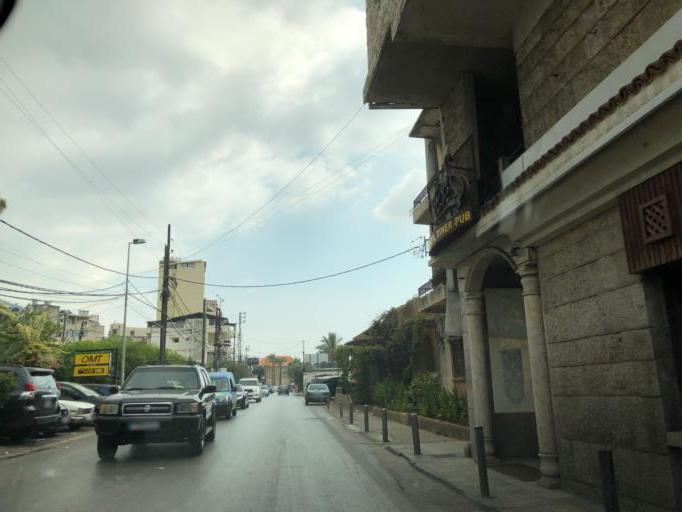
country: LB
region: Mont-Liban
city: Djounie
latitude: 33.9938
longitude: 35.6405
